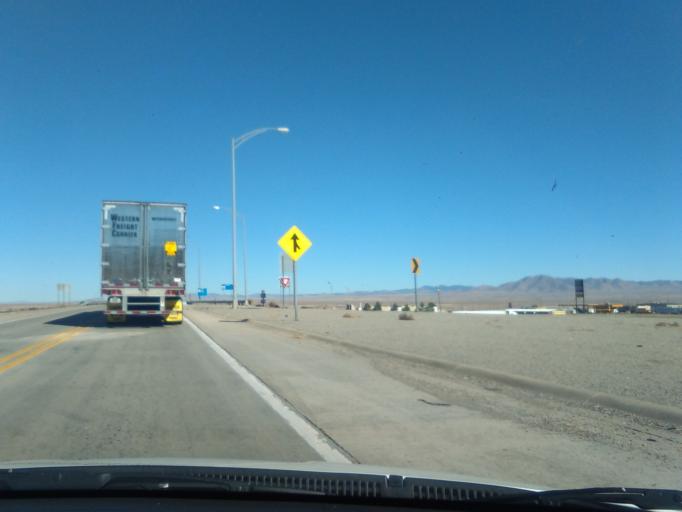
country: US
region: New Mexico
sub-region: Hidalgo County
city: Lordsburg
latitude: 32.3512
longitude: -108.7413
